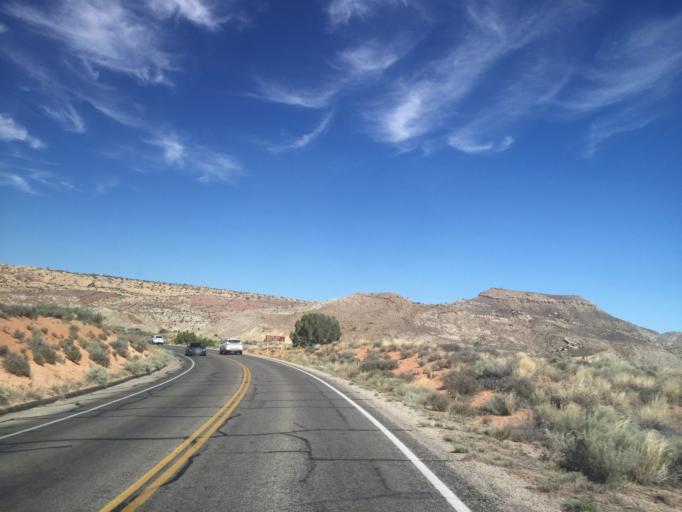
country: US
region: Utah
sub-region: Grand County
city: Moab
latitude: 38.7269
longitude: -109.5391
